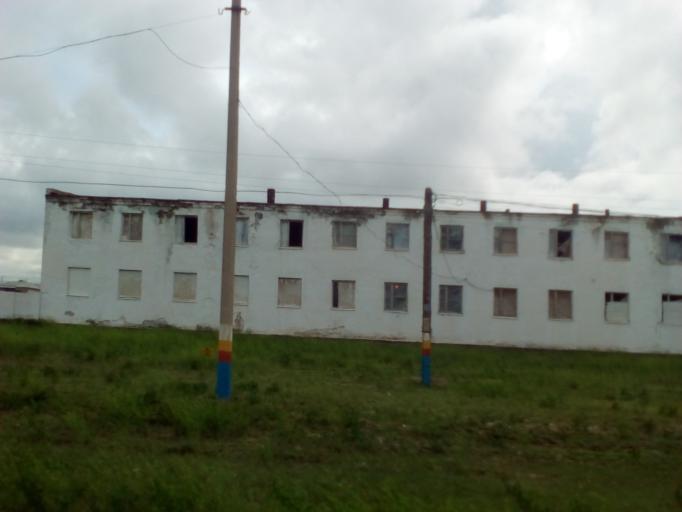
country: KZ
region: Ongtustik Qazaqstan
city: Sholaqqkorghan
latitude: 43.7511
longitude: 69.1954
